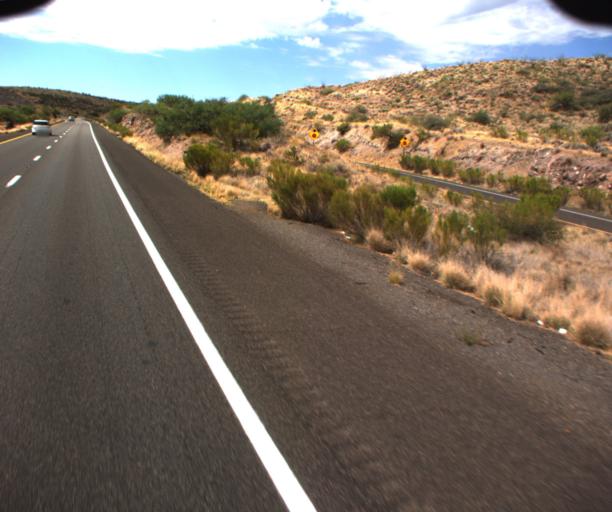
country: US
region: Arizona
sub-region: Yavapai County
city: Cordes Lakes
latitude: 34.2384
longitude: -112.1155
